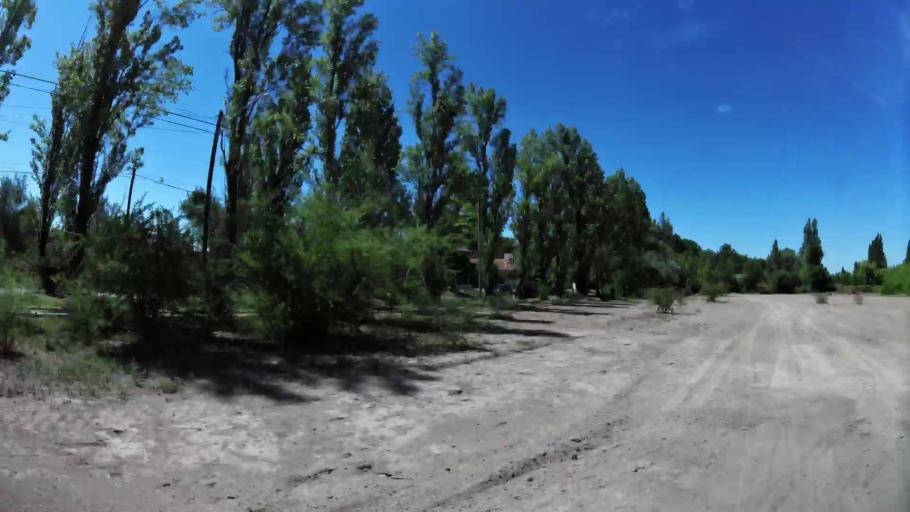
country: AR
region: Mendoza
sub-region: Departamento de Godoy Cruz
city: Godoy Cruz
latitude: -32.9643
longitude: -68.8613
